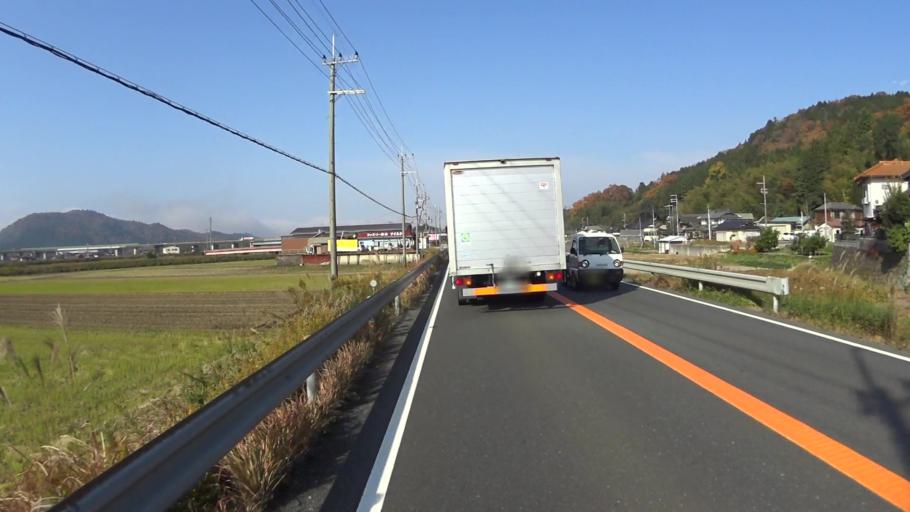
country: JP
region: Kyoto
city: Ayabe
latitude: 35.2626
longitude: 135.1887
